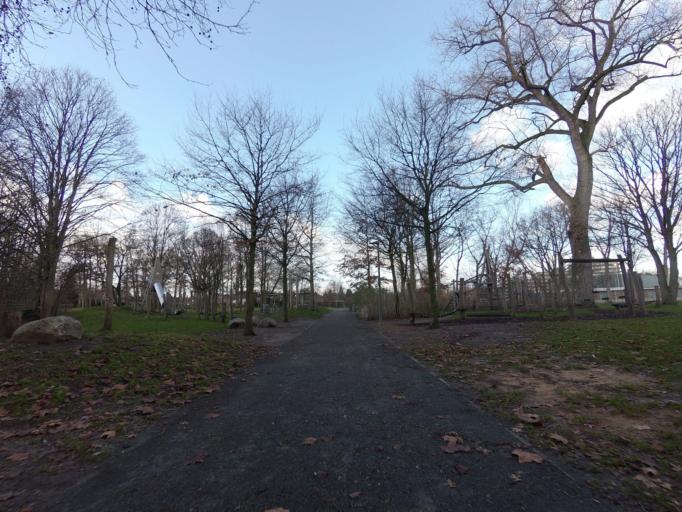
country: BE
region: Flanders
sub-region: Provincie Antwerpen
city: Kapellen
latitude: 51.2781
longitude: 4.4149
